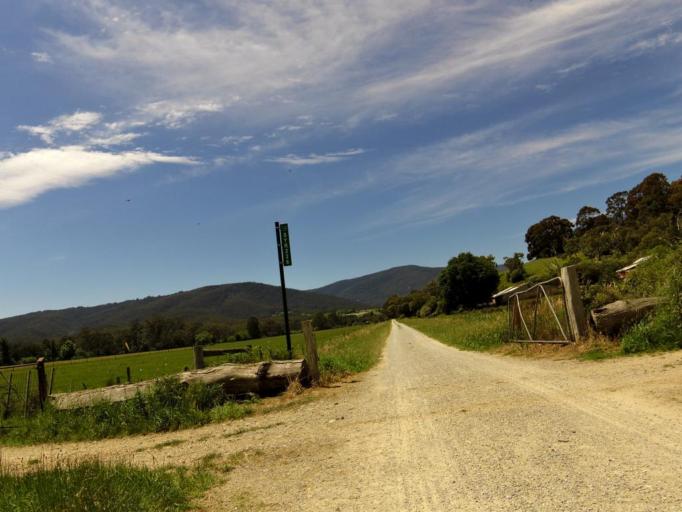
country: AU
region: Victoria
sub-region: Yarra Ranges
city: Woori Yallock
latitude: -37.7683
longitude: 145.5431
